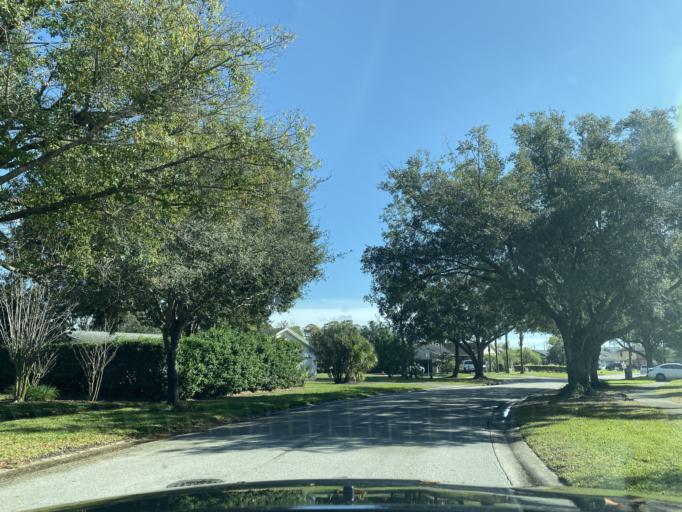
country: US
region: Florida
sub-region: Orange County
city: Azalea Park
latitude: 28.5258
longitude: -81.2591
